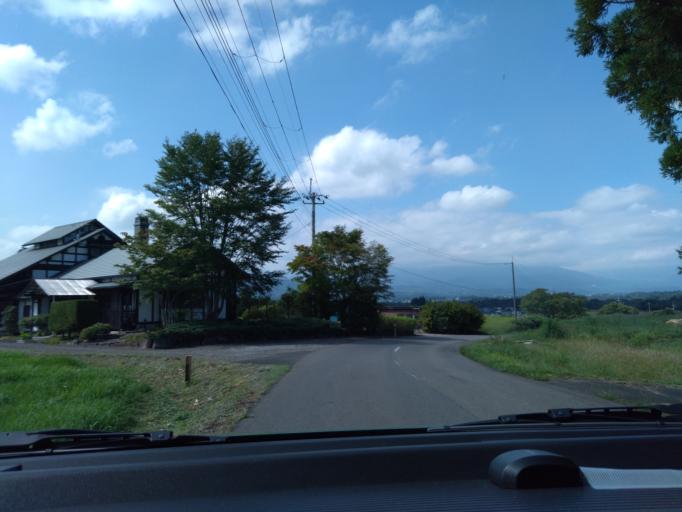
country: JP
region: Iwate
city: Shizukuishi
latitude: 39.6791
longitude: 140.9595
